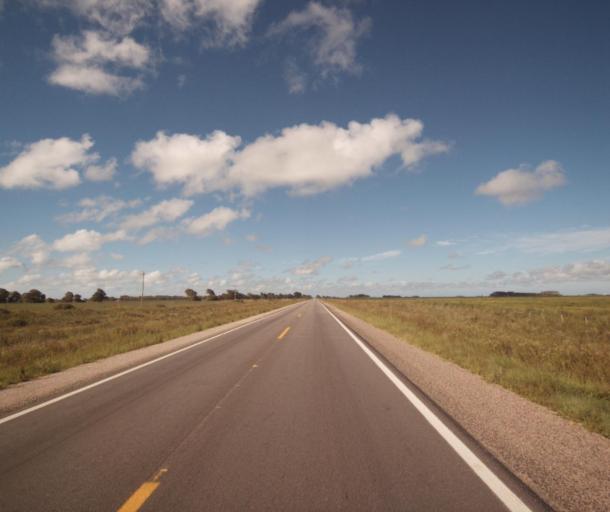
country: UY
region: Cerro Largo
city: Rio Branco
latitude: -32.9545
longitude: -52.7797
